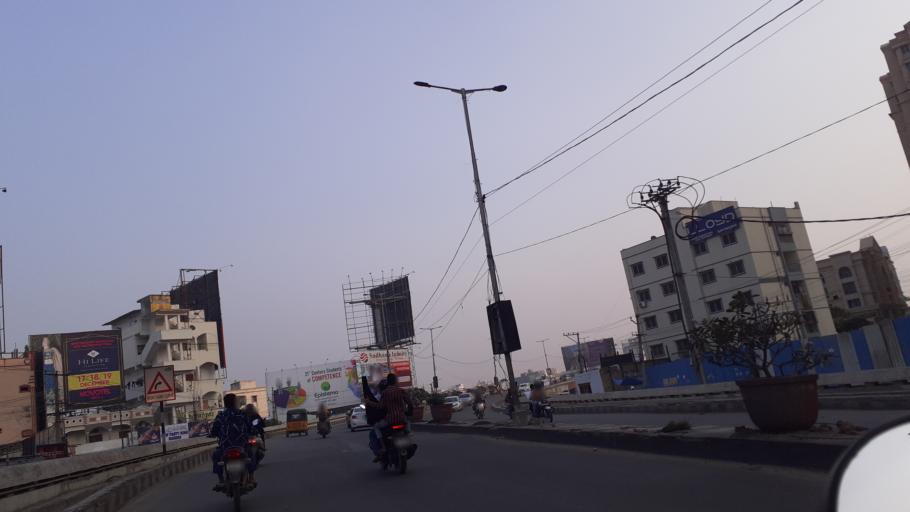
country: IN
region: Telangana
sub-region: Rangareddi
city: Kukatpalli
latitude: 17.4853
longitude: 78.3597
